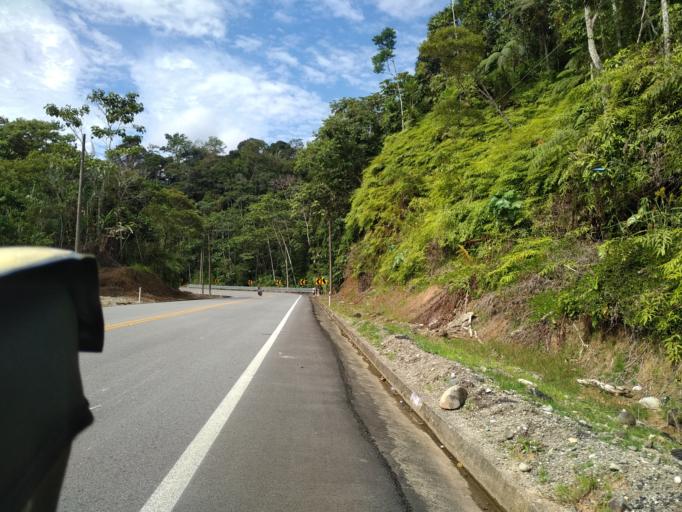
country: EC
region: Napo
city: Tena
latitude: -1.1162
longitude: -77.8090
